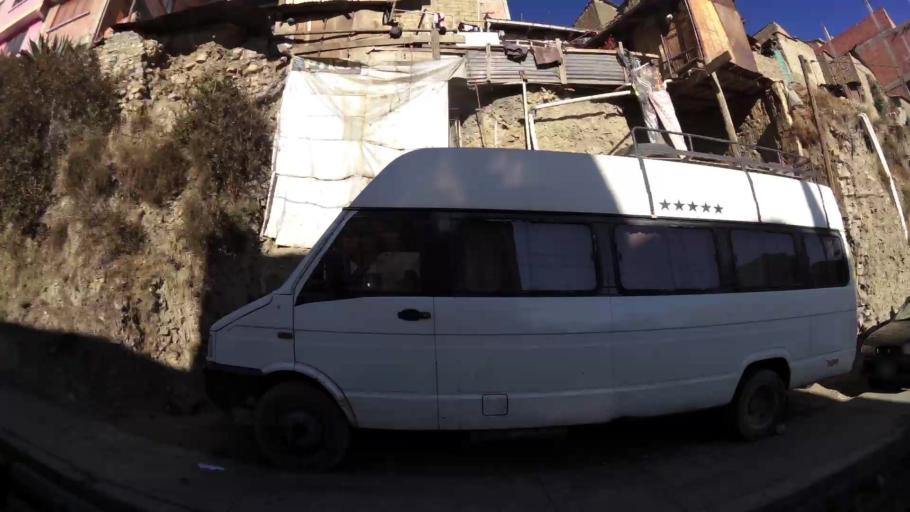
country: BO
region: La Paz
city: La Paz
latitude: -16.5102
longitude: -68.1541
